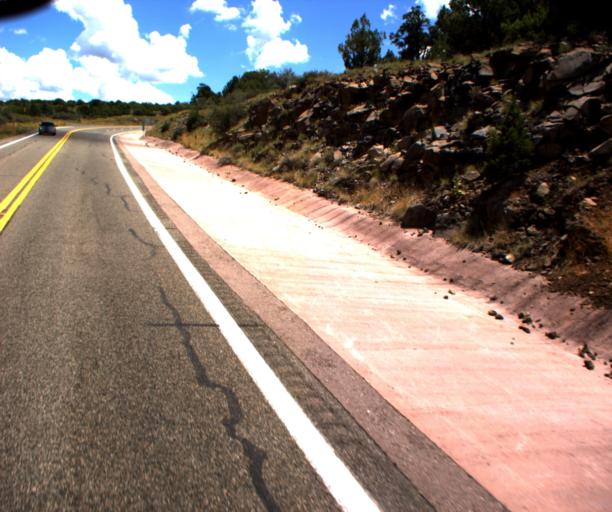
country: US
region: Arizona
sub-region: Yavapai County
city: Lake Montezuma
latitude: 34.4995
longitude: -111.6374
